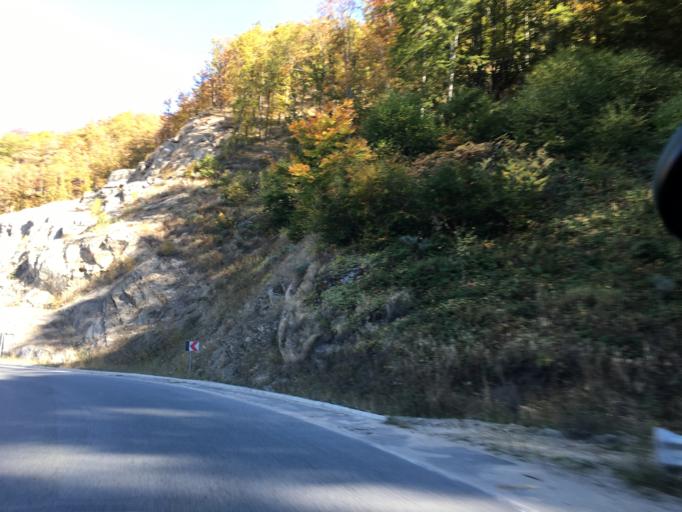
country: BG
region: Smolyan
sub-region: Obshtina Devin
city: Devin
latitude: 41.7819
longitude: 24.4580
